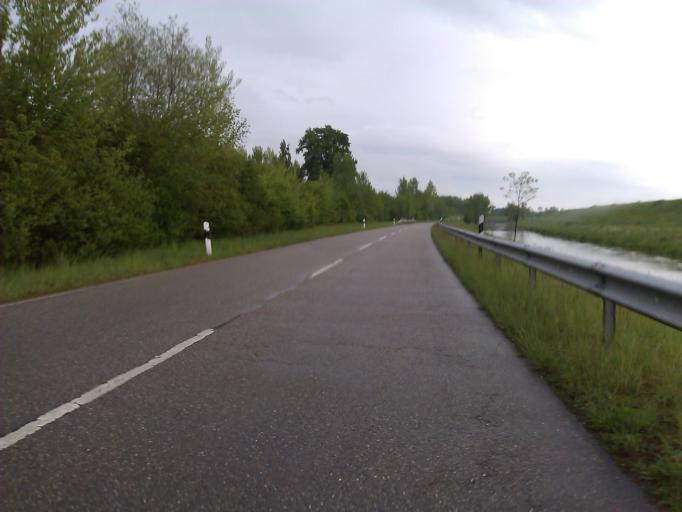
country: DE
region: Baden-Wuerttemberg
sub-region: Karlsruhe Region
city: Rheinmuenster
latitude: 48.7682
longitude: 8.0255
